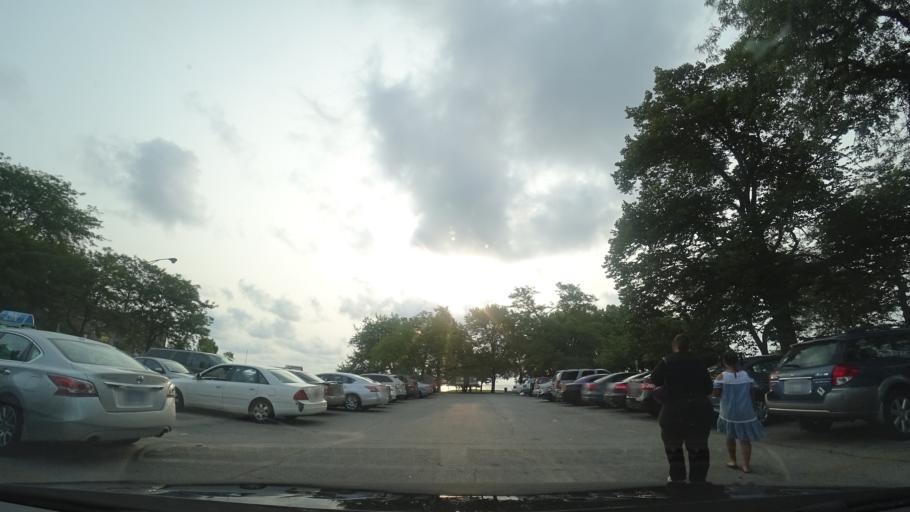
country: US
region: Illinois
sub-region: Cook County
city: Evanston
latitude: 42.0127
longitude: -87.6629
